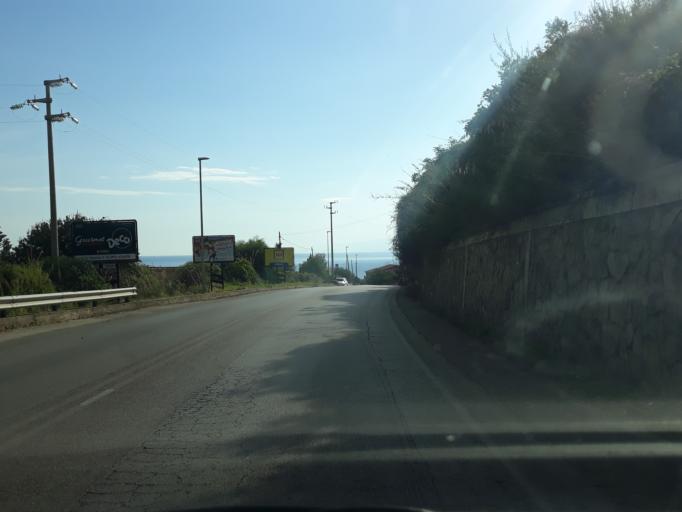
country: IT
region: Sicily
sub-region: Palermo
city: Cefalu
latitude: 38.0326
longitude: 14.0325
